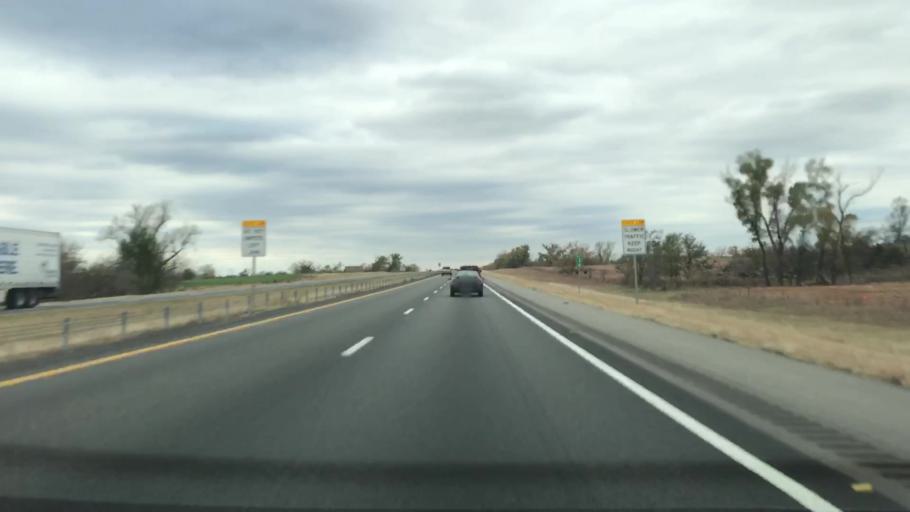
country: US
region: Oklahoma
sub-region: Beckham County
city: Elk City
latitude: 35.3859
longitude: -99.4864
